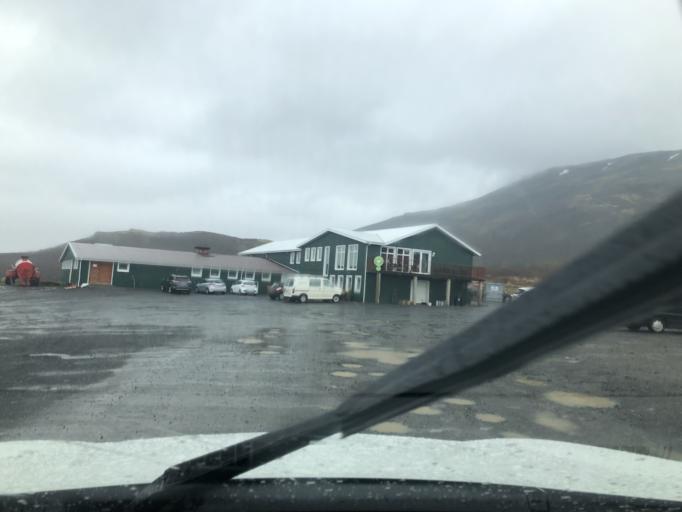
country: IS
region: South
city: Selfoss
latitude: 64.2426
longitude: -20.5505
